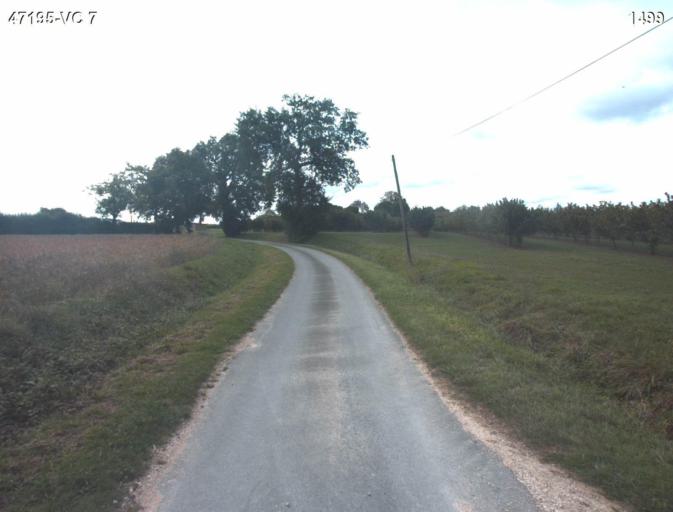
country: FR
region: Aquitaine
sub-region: Departement du Lot-et-Garonne
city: Nerac
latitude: 44.1033
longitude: 0.3400
